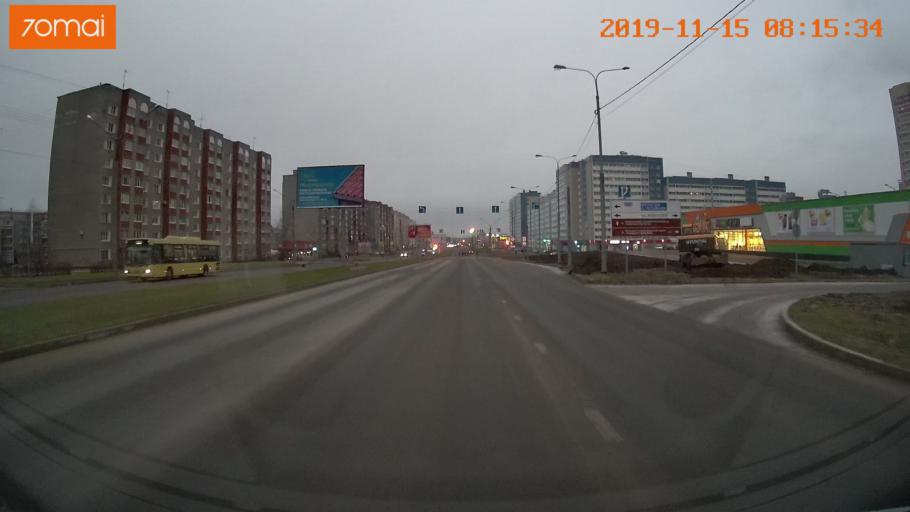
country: RU
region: Vologda
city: Cherepovets
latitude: 59.0835
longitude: 37.9215
